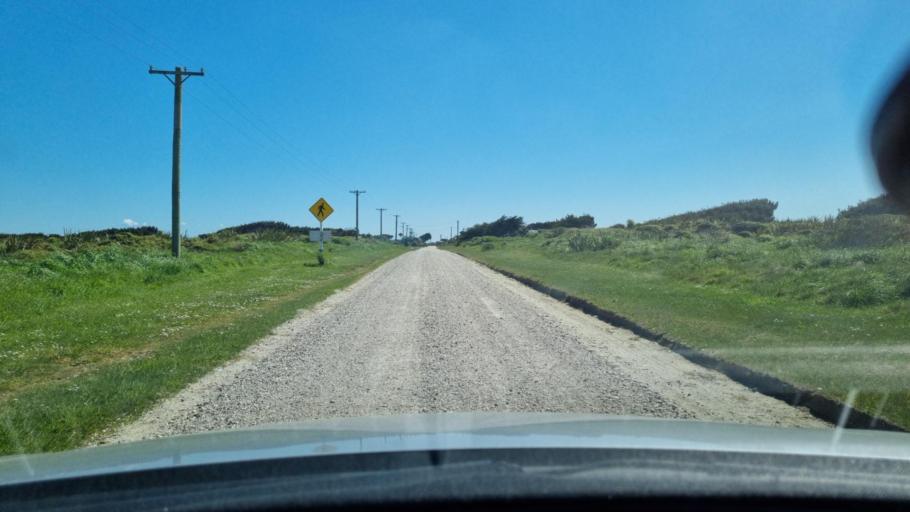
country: NZ
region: Southland
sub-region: Invercargill City
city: Invercargill
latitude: -46.4330
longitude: 168.2354
